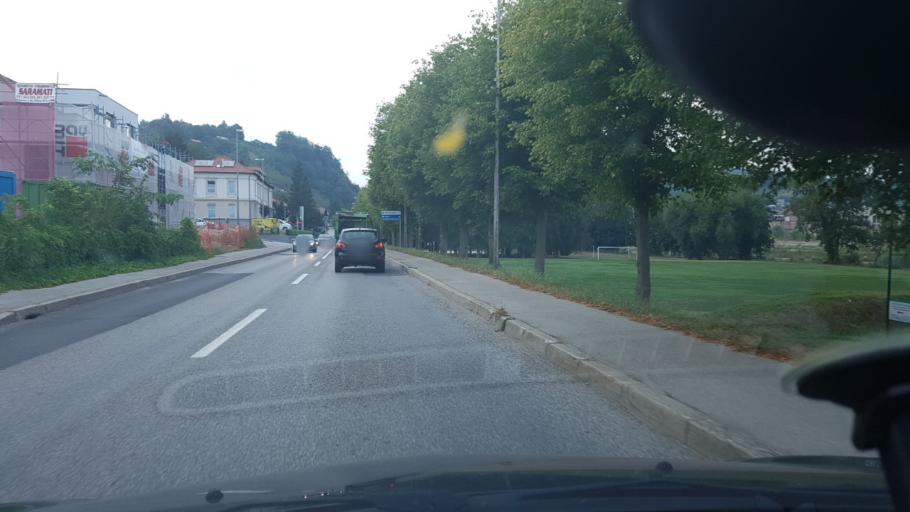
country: SI
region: Krsko
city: Krsko
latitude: 45.9507
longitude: 15.4870
